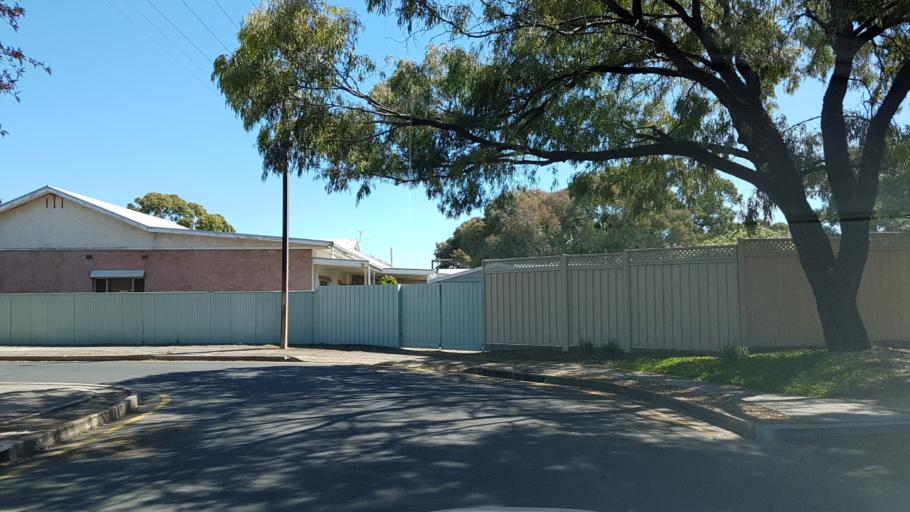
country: AU
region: South Australia
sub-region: Unley
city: Forestville
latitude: -34.9609
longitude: 138.5678
